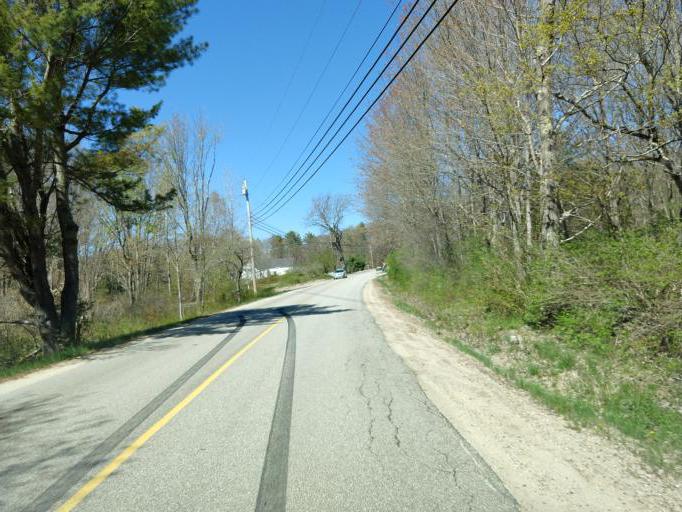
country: US
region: Maine
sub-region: York County
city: Arundel
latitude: 43.3882
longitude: -70.4612
